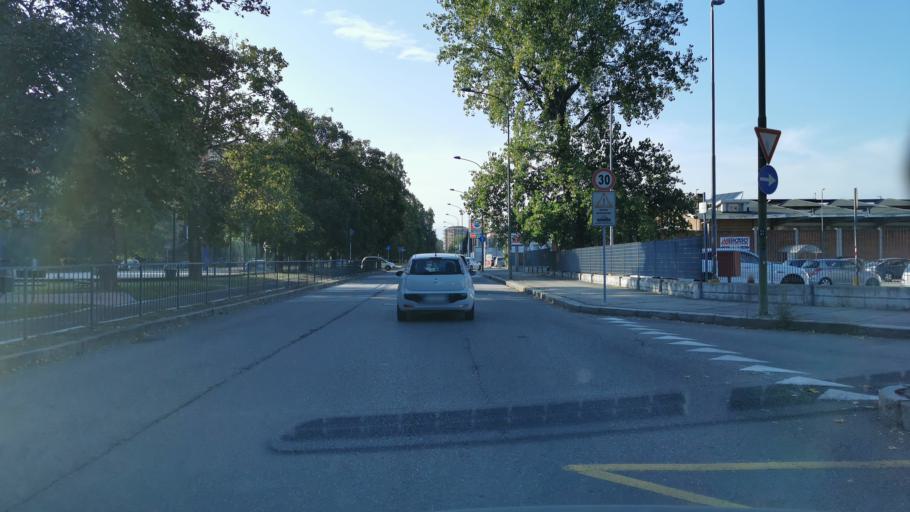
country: IT
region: Piedmont
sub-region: Provincia di Torino
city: Turin
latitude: 45.0972
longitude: 7.7099
